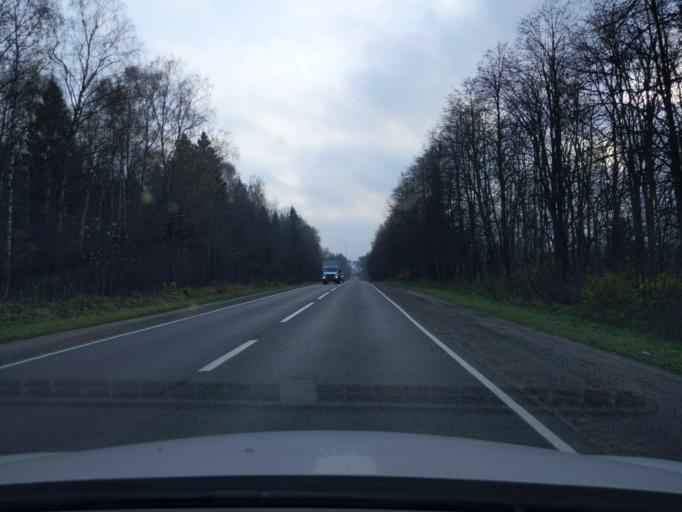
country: RU
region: Moskovskaya
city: Ashukino
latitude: 56.1478
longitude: 37.9881
